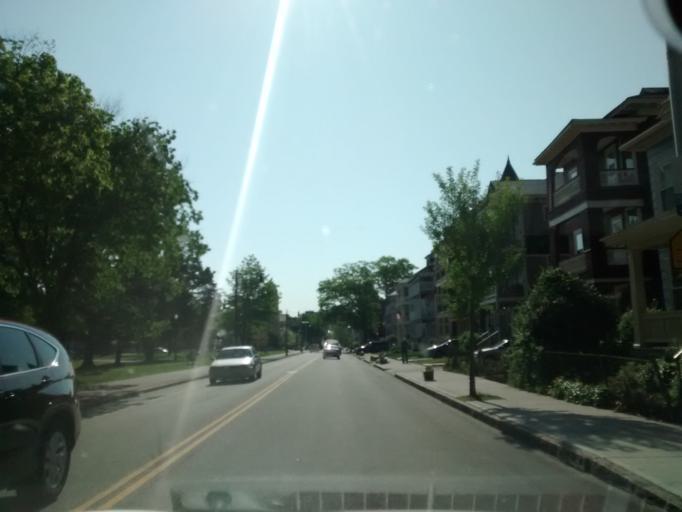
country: US
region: Massachusetts
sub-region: Worcester County
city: Worcester
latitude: 42.2663
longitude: -71.8175
